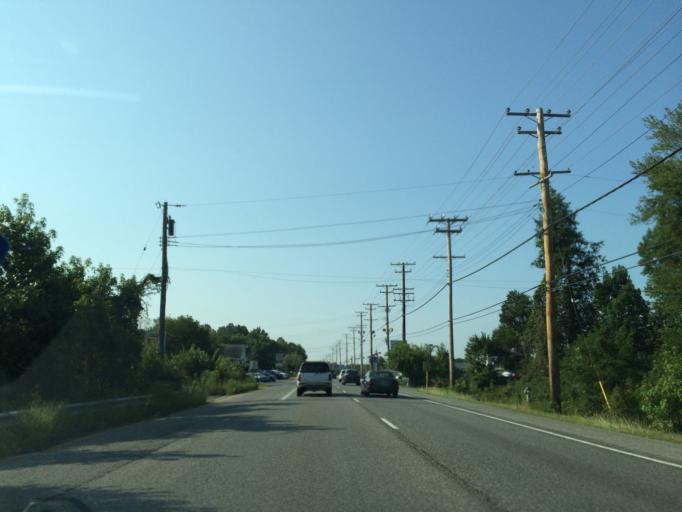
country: US
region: Maryland
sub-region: Prince George's County
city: Bowie
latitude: 38.9244
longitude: -76.7173
